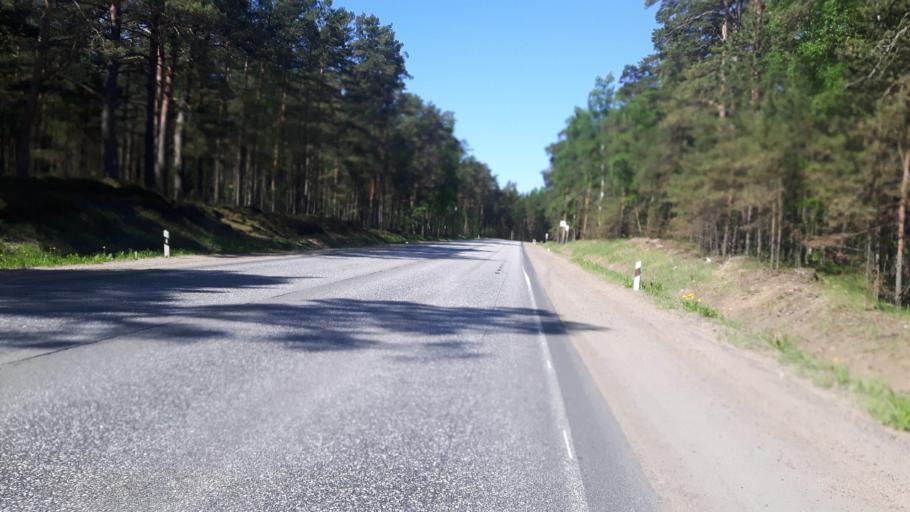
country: RU
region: Leningrad
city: Lebyazh'ye
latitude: 59.9571
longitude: 29.4617
